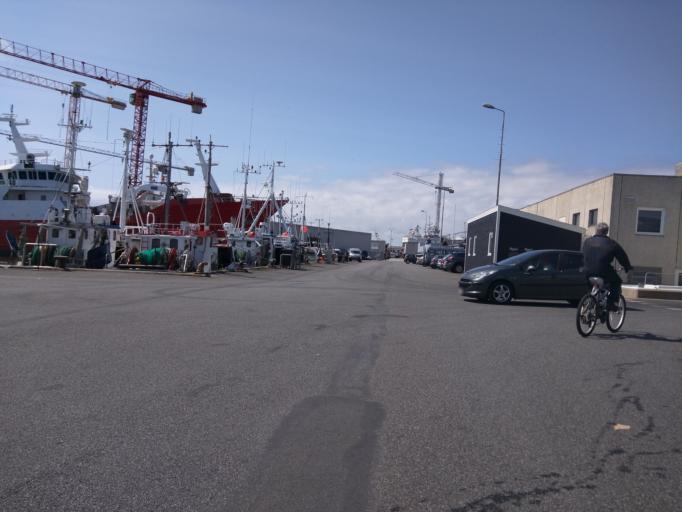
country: DK
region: North Denmark
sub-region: Frederikshavn Kommune
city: Skagen
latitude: 57.7180
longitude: 10.5860
